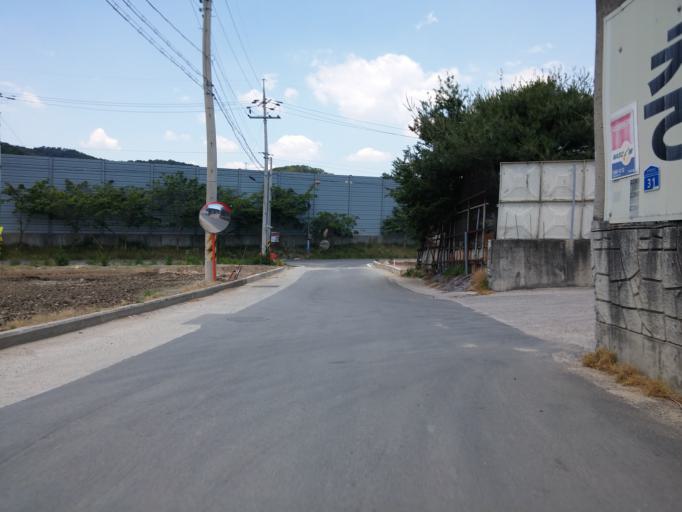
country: KR
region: Chungcheongbuk-do
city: Cheongju-si
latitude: 36.5559
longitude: 127.4333
